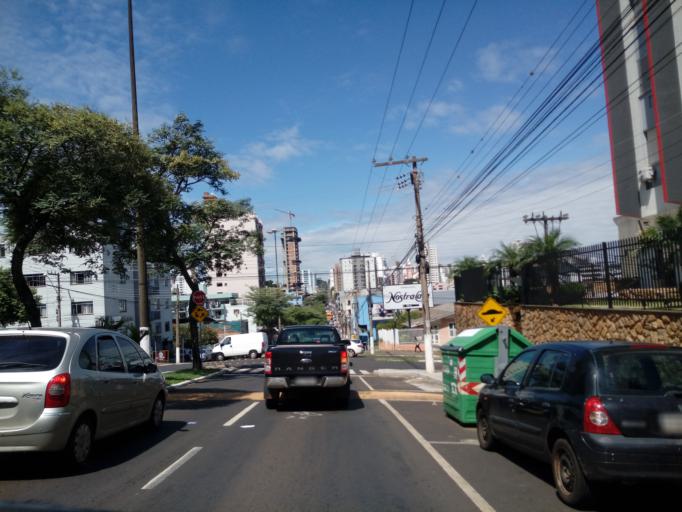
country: BR
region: Santa Catarina
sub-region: Chapeco
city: Chapeco
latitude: -27.0971
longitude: -52.6144
